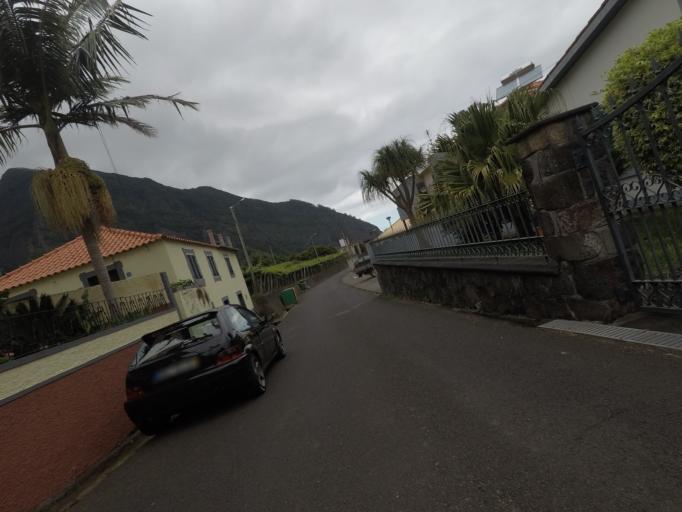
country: PT
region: Madeira
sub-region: Sao Vicente
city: Sao Vicente
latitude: 32.7912
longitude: -17.0392
